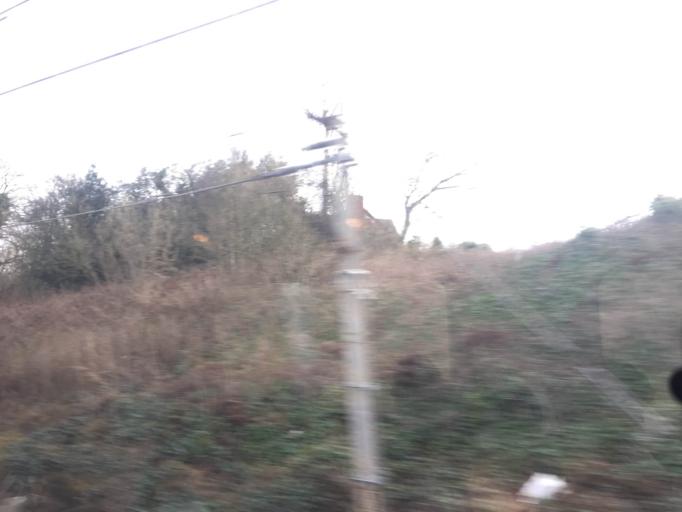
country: GB
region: England
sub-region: Borough of Wigan
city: Ince-in-Makerfield
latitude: 53.5751
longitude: -2.6397
